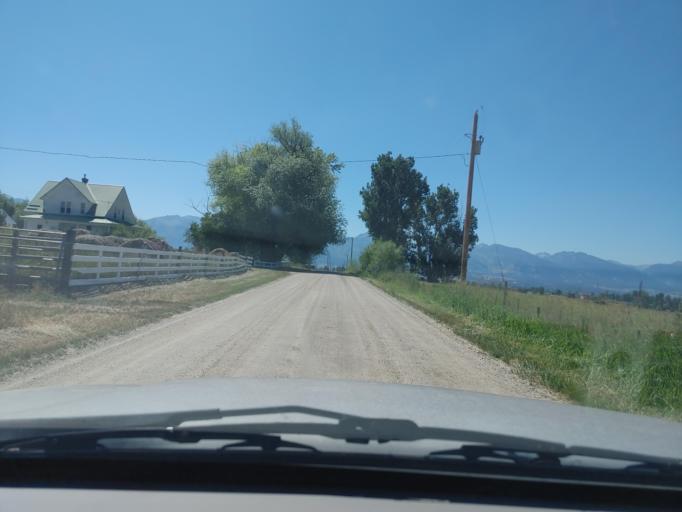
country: US
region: Montana
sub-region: Ravalli County
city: Hamilton
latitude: 46.2766
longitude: -114.0279
